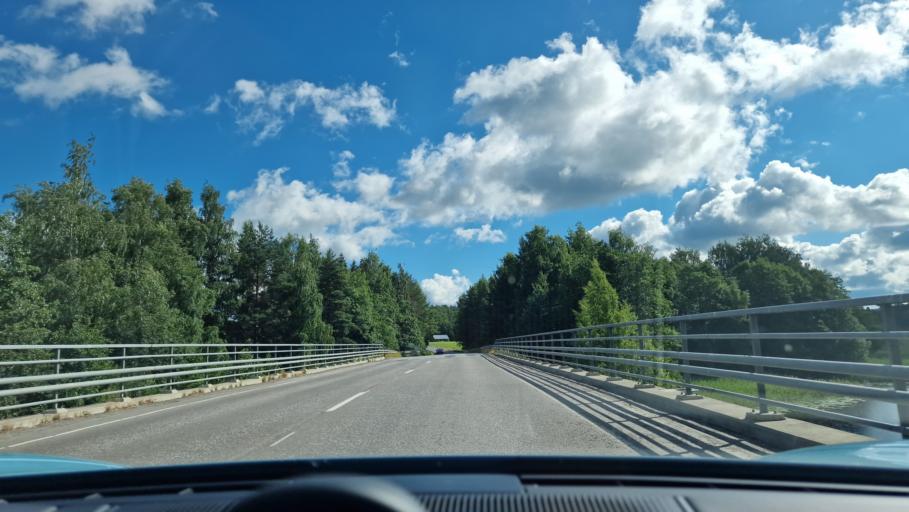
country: FI
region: Pirkanmaa
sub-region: Tampere
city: Paelkaene
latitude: 61.2936
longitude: 24.2970
